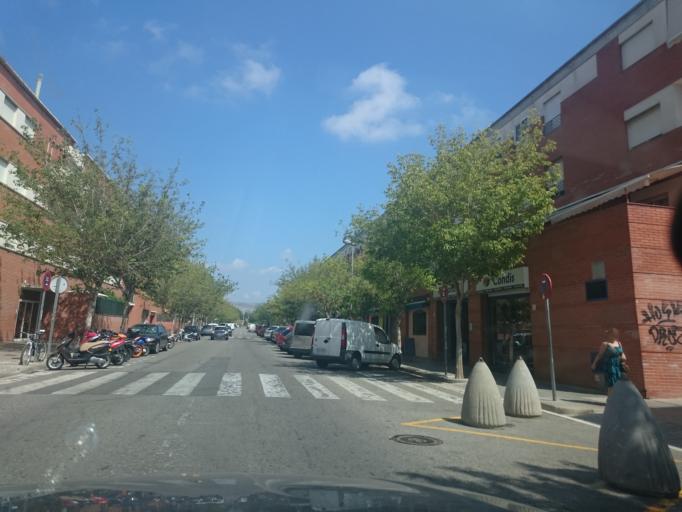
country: ES
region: Catalonia
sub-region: Provincia de Barcelona
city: Vilanova i la Geltru
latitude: 41.2221
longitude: 1.7108
